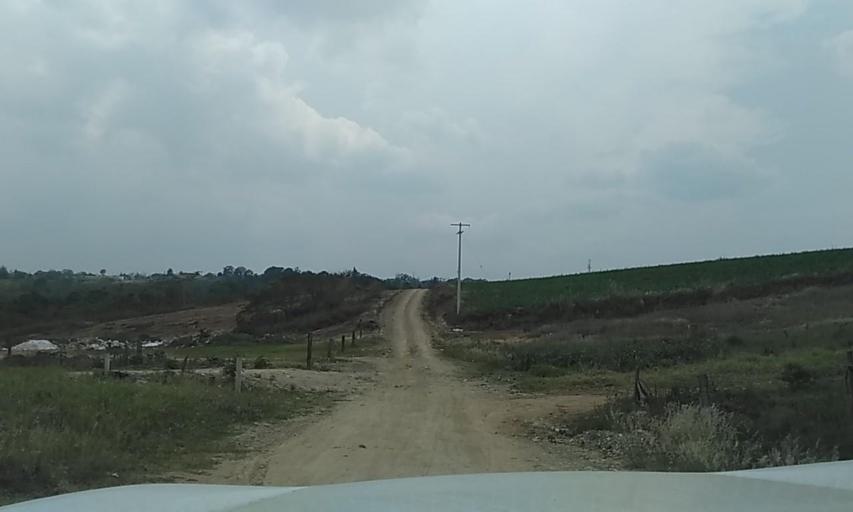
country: MX
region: Veracruz
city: El Castillo
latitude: 19.5396
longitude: -96.8768
